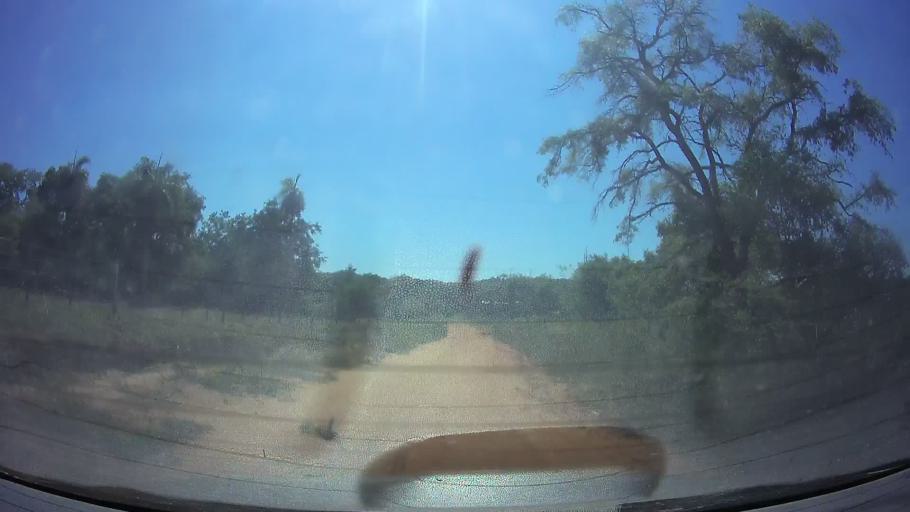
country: PY
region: Central
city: Limpio
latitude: -25.2380
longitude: -57.4409
